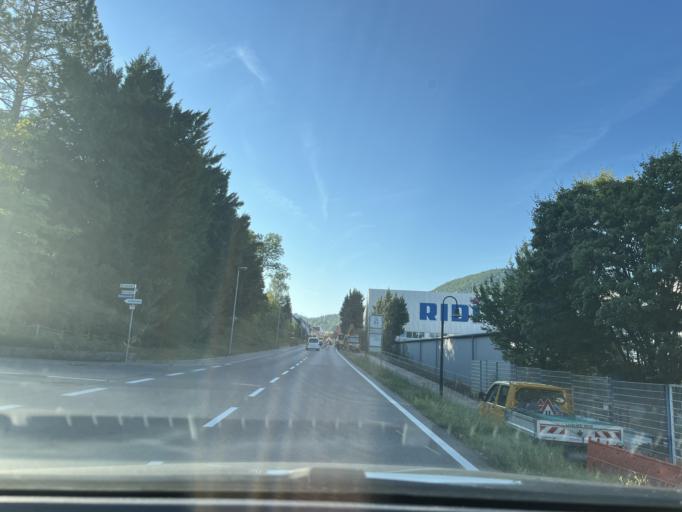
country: DE
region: Baden-Wuerttemberg
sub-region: Tuebingen Region
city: Jungingen
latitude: 48.3304
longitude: 9.0369
